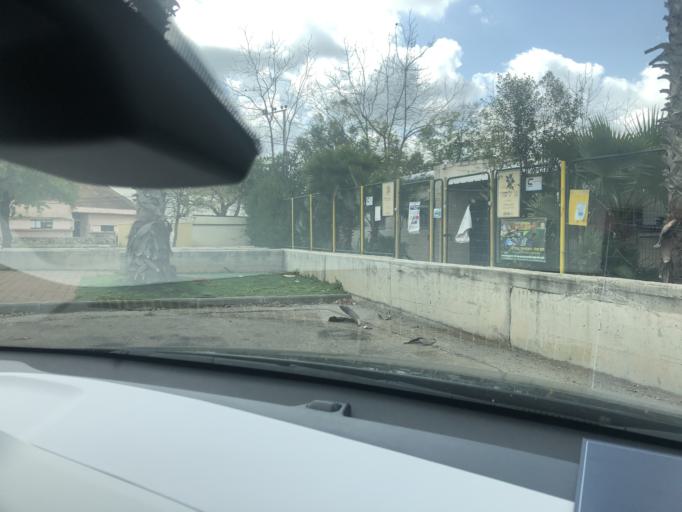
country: IL
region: Haifa
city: Hadera
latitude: 32.4665
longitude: 34.9568
